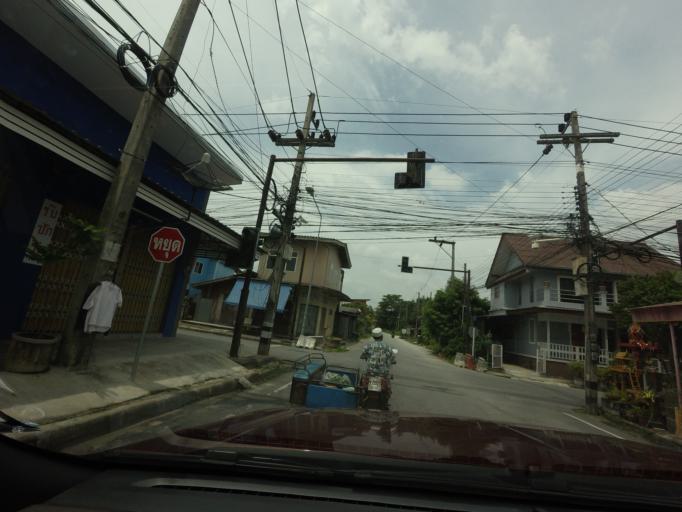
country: TH
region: Yala
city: Yala
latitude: 6.5606
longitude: 101.2981
